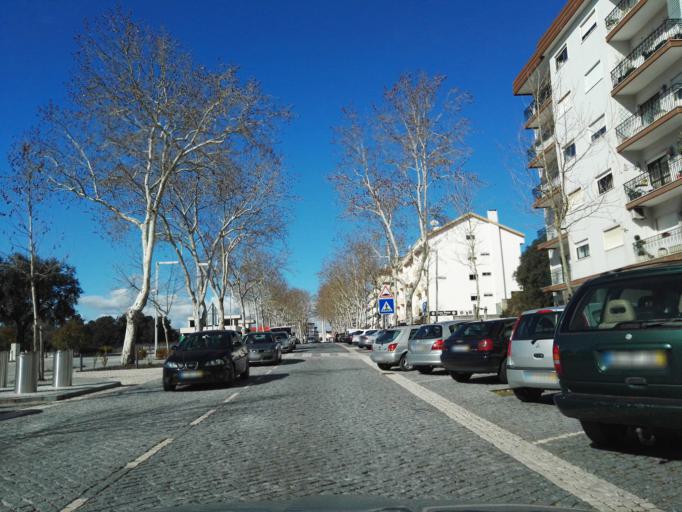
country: PT
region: Santarem
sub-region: Ourem
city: Fatima
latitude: 39.6322
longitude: -8.6810
